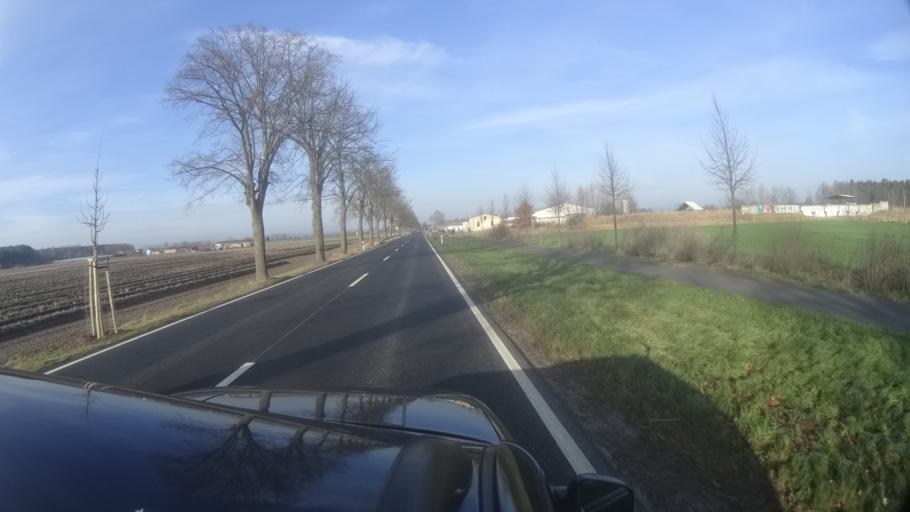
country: DE
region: Brandenburg
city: Kremmen
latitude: 52.7447
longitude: 13.0494
